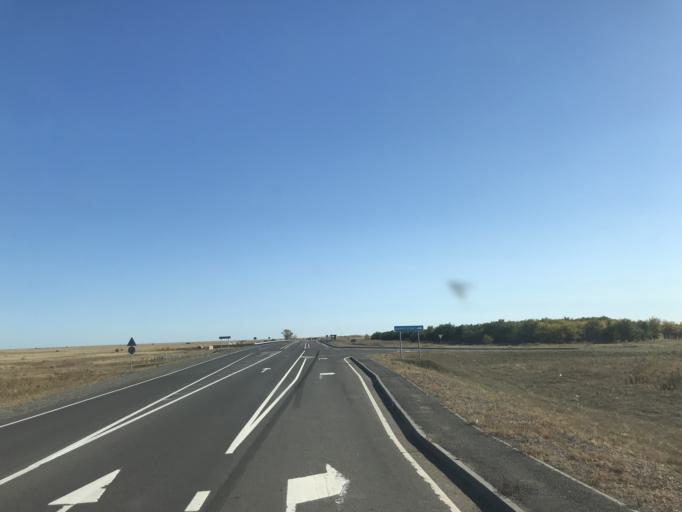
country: KZ
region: Pavlodar
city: Aksu
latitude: 52.0184
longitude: 77.2325
